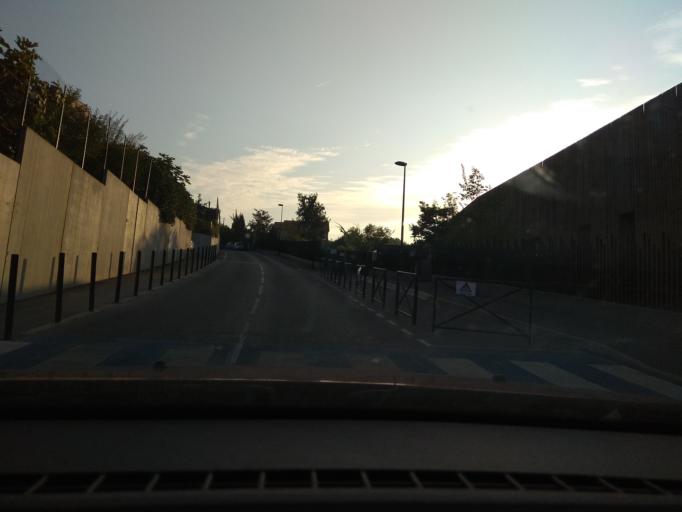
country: FR
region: Provence-Alpes-Cote d'Azur
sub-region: Departement des Alpes-Maritimes
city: Villeneuve-Loubet
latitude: 43.6757
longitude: 7.1107
